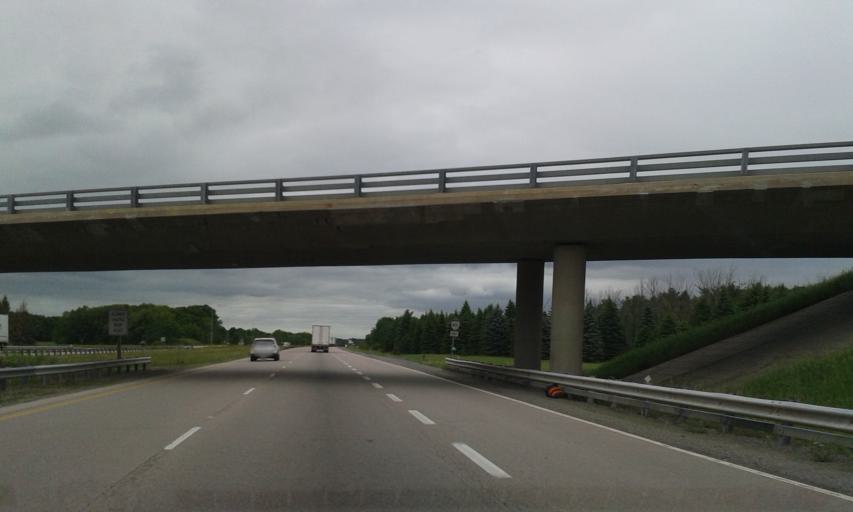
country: US
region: New York
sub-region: Jefferson County
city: Alexandria Bay
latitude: 44.4736
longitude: -75.8701
